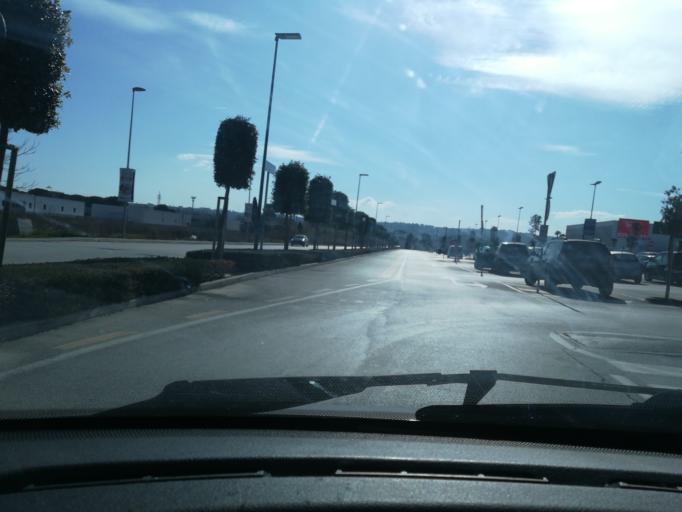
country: IT
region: The Marches
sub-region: Provincia di Macerata
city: Santa Maria Apparente
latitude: 43.2931
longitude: 13.7028
